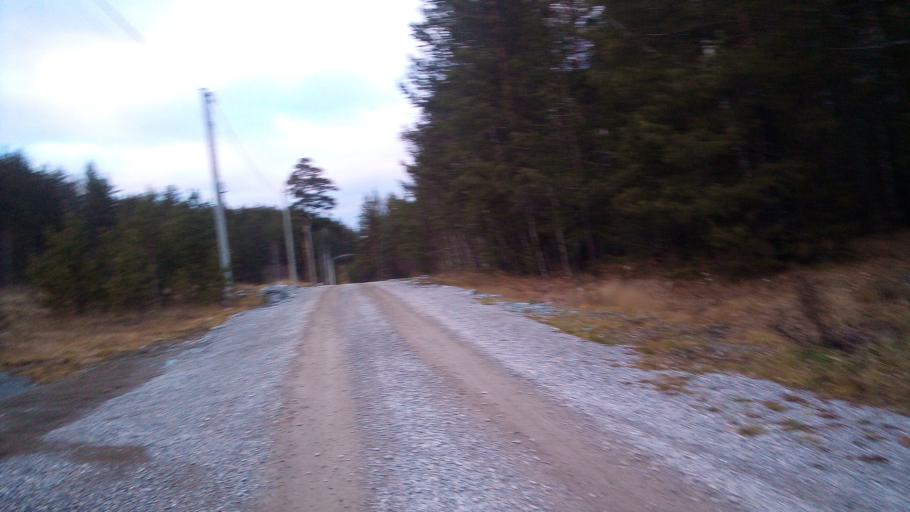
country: RU
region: Chelyabinsk
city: Turgoyak
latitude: 55.1775
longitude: 60.1311
